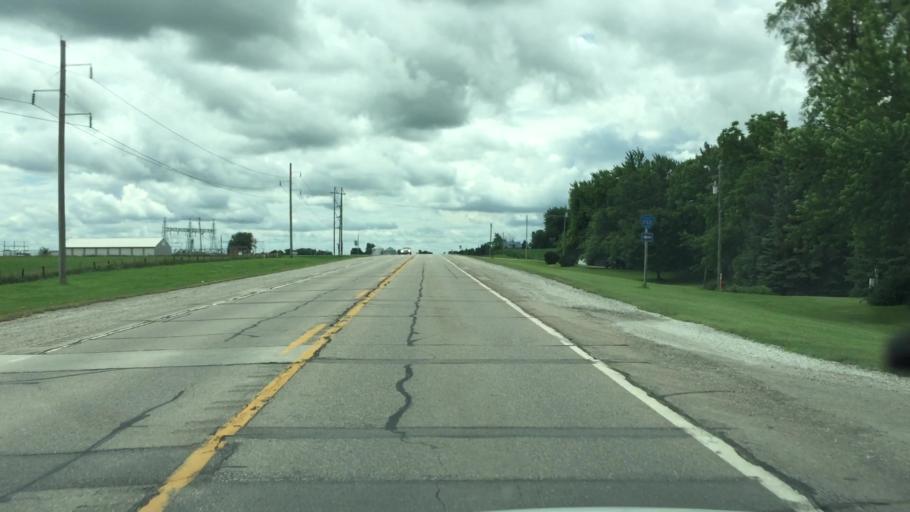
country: US
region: Iowa
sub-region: Jasper County
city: Monroe
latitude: 41.5754
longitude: -93.0971
